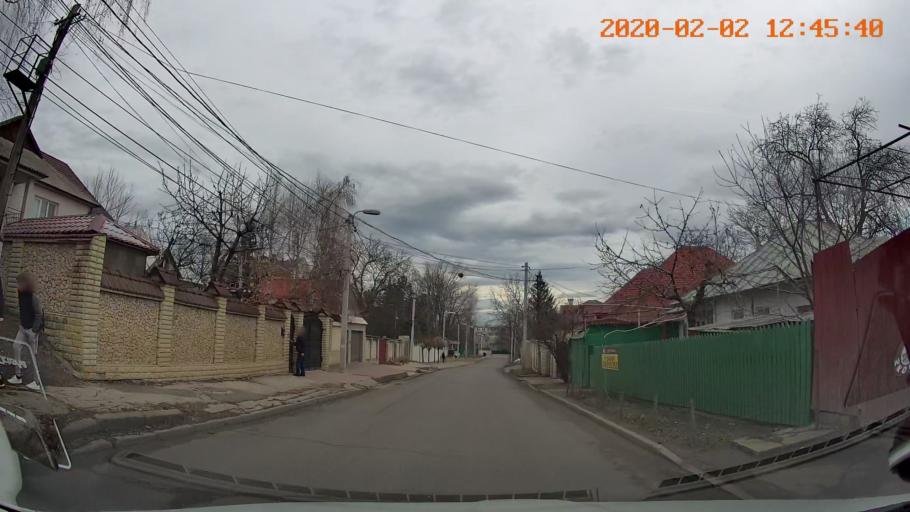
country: MD
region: Chisinau
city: Chisinau
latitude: 47.0061
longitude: 28.8149
